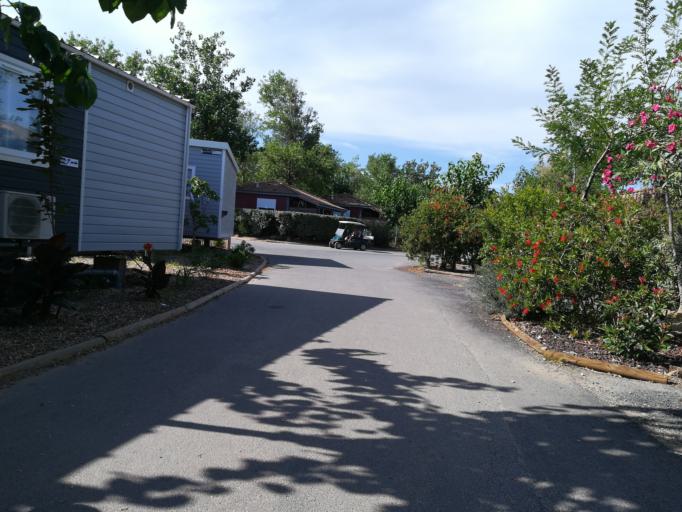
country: FR
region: Languedoc-Roussillon
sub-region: Departement de l'Herault
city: Portiragnes
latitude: 43.2803
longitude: 3.3664
